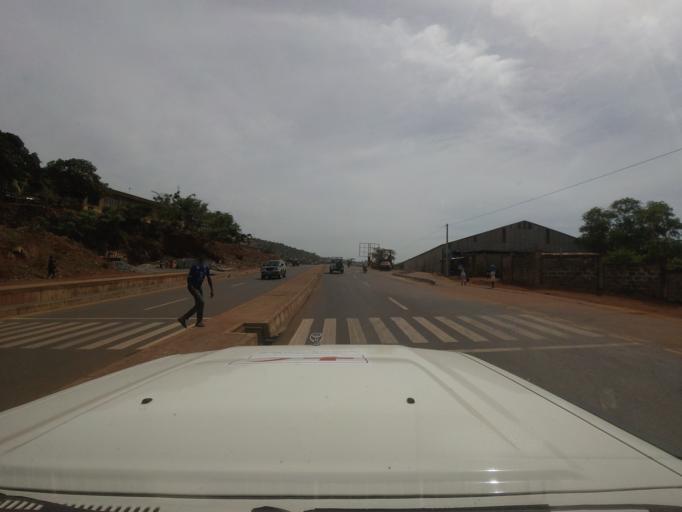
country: SL
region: Western Area
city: Freetown
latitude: 8.4751
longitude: -13.2339
